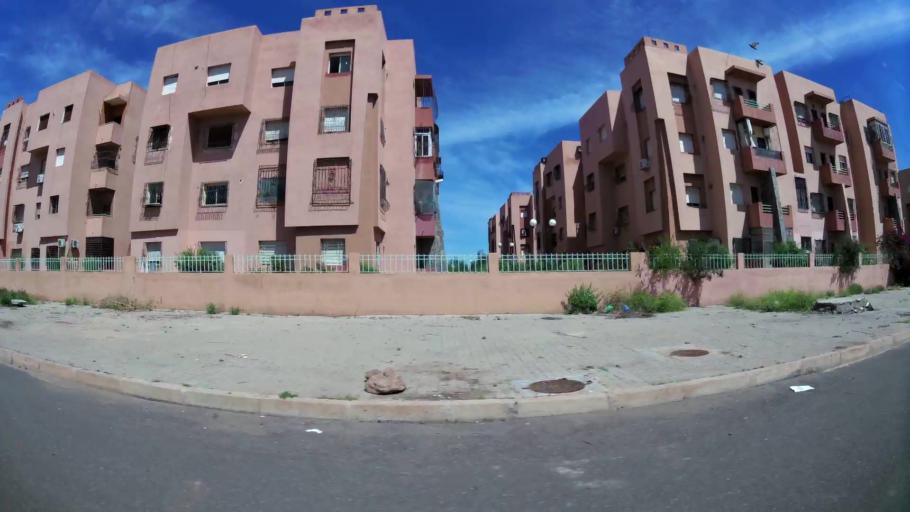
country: MA
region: Marrakech-Tensift-Al Haouz
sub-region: Marrakech
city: Marrakesh
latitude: 31.6459
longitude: -8.0815
